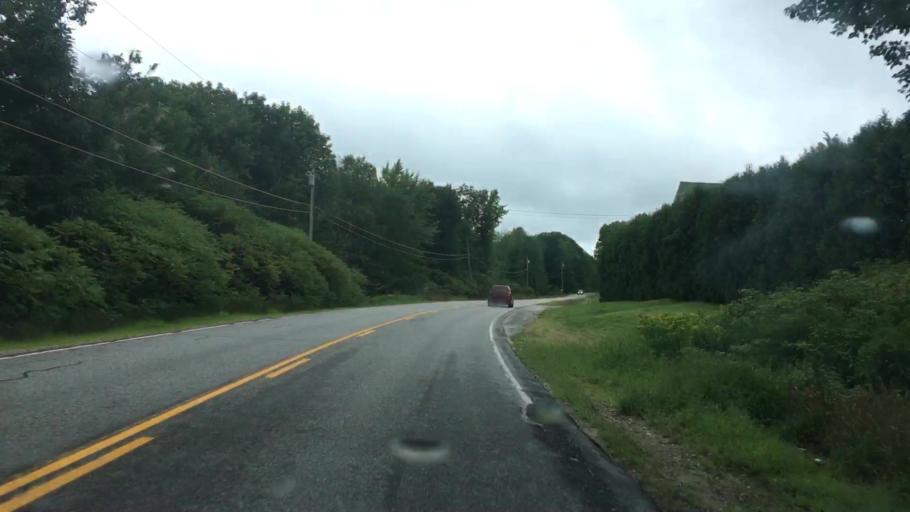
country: US
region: Maine
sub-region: Oxford County
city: Brownfield
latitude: 43.9584
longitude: -70.8991
